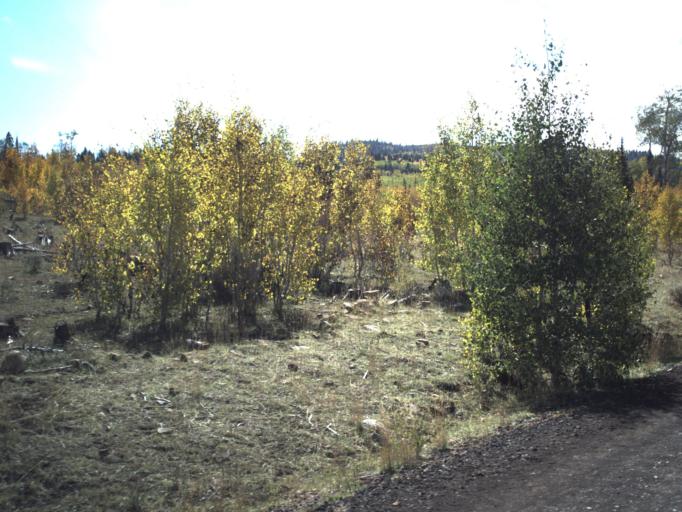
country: US
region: Utah
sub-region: Piute County
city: Junction
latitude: 38.2536
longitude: -112.3347
